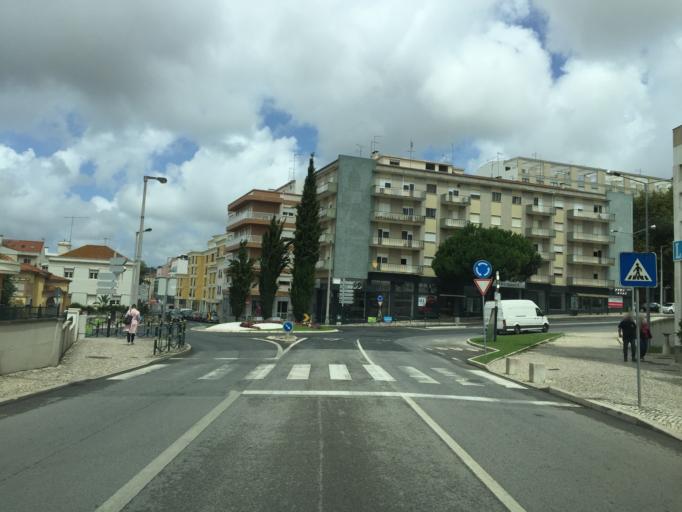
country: PT
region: Lisbon
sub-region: Torres Vedras
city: Torres Vedras
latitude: 39.0867
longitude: -9.2566
